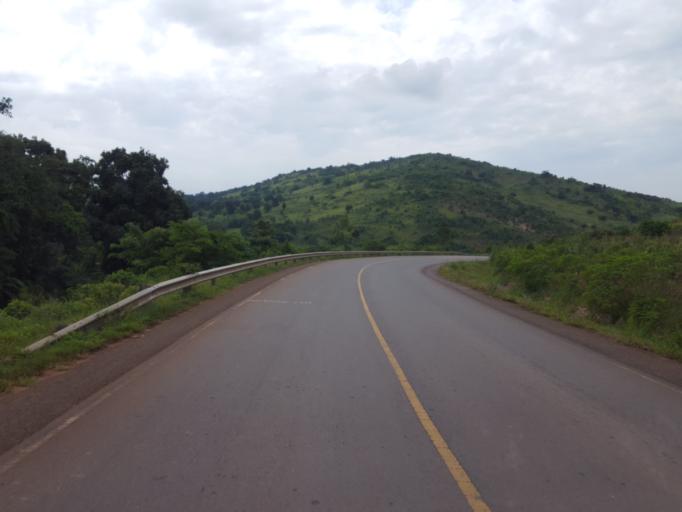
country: UG
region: Central Region
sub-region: Mityana District
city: Mityana
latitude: 0.6250
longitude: 32.1325
